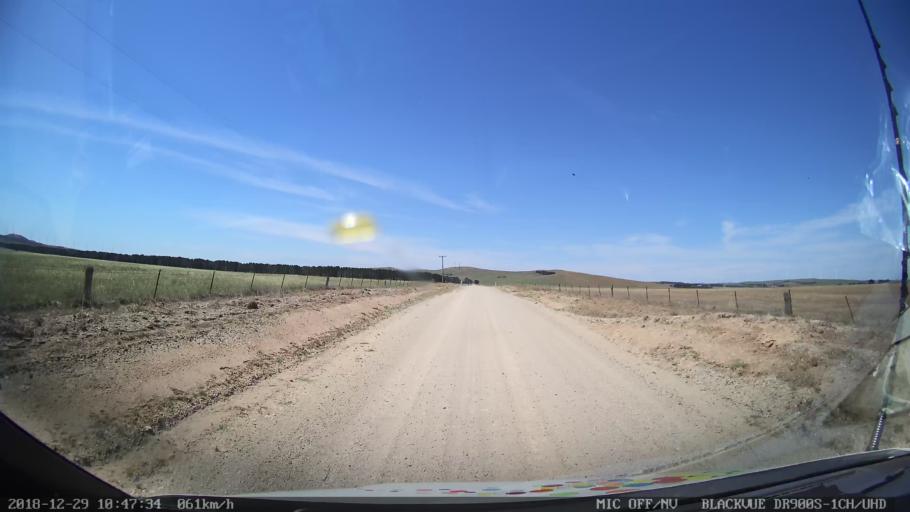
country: AU
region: New South Wales
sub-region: Palerang
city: Bungendore
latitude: -35.0605
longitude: 149.5160
